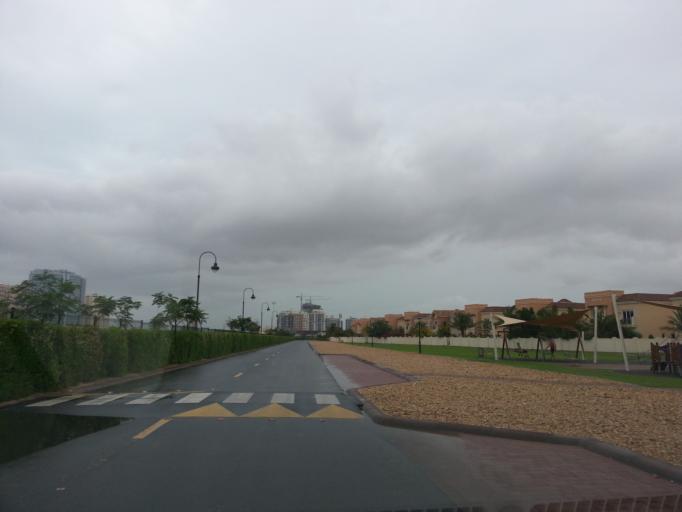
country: AE
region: Dubai
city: Dubai
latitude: 25.0278
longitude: 55.2097
